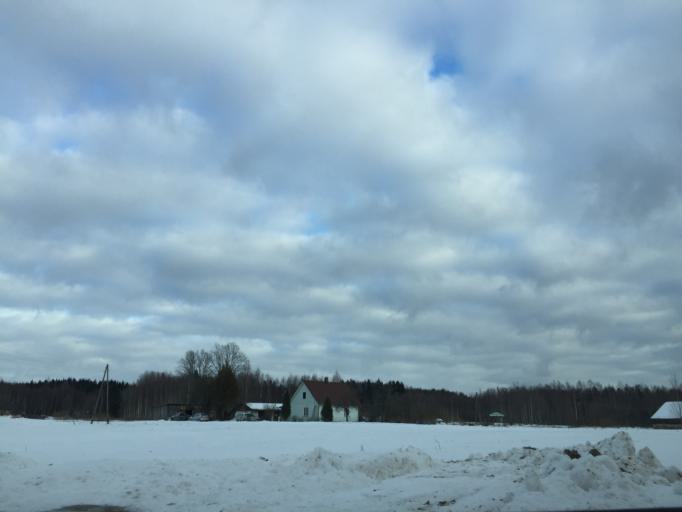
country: LV
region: Lielvarde
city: Lielvarde
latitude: 56.5763
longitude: 24.7939
